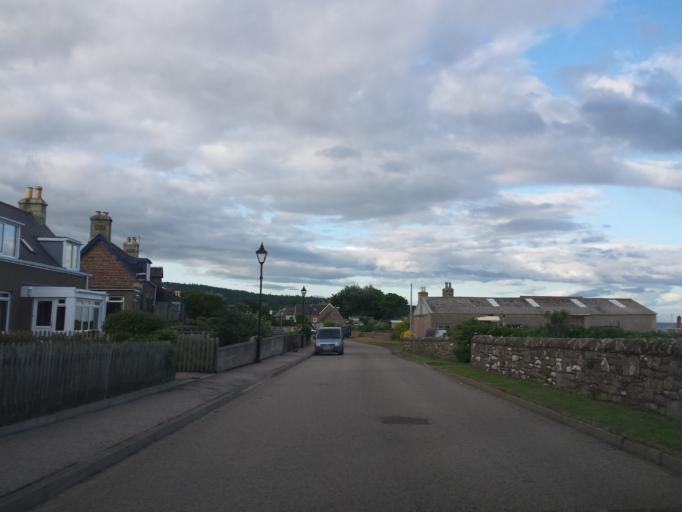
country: GB
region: Scotland
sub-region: Highland
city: Golspie
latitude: 57.9700
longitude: -3.9832
